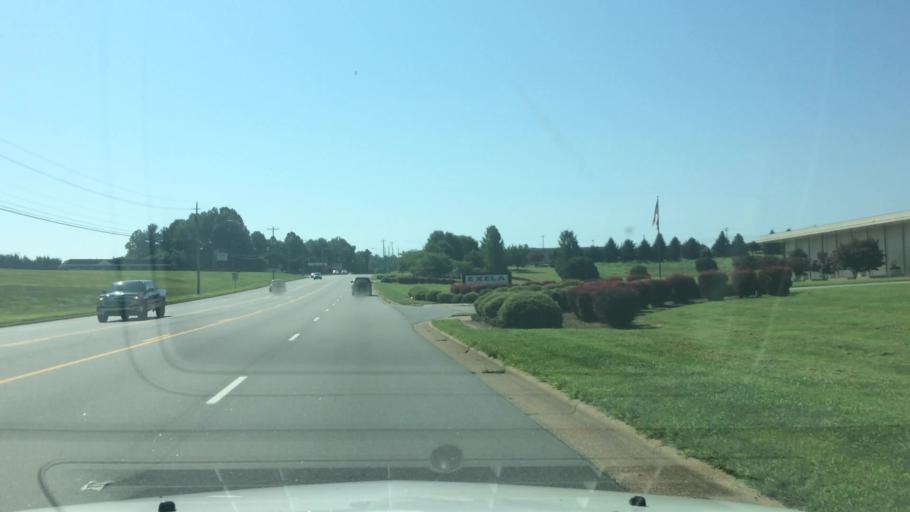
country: US
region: North Carolina
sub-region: Caldwell County
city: Lenoir
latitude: 35.9343
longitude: -81.5321
